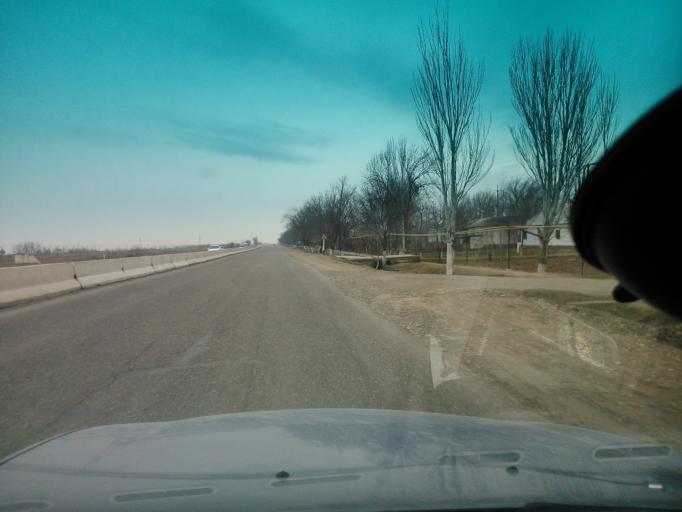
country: UZ
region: Sirdaryo
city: Guliston
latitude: 40.4160
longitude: 68.7858
